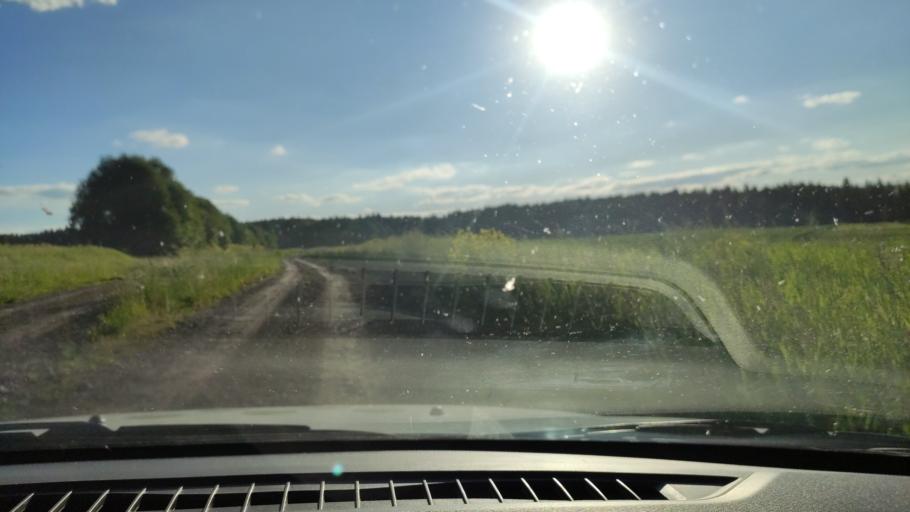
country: RU
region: Perm
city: Orda
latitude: 57.3008
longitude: 56.5971
